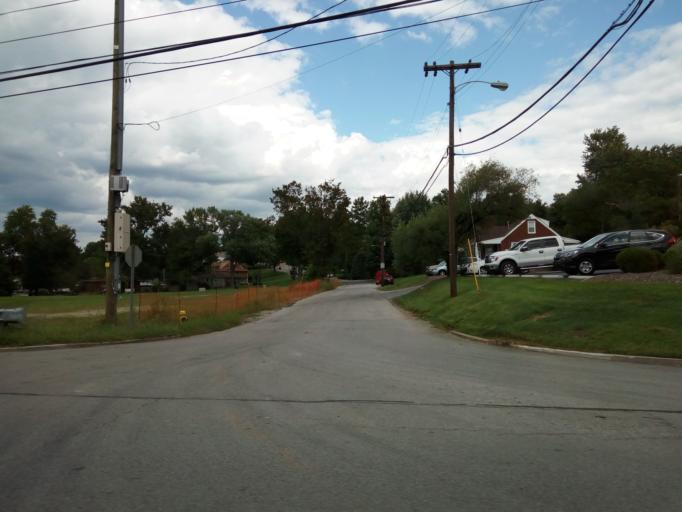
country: US
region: Kentucky
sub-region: Jefferson County
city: Audubon Park
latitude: 38.2092
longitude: -85.7163
